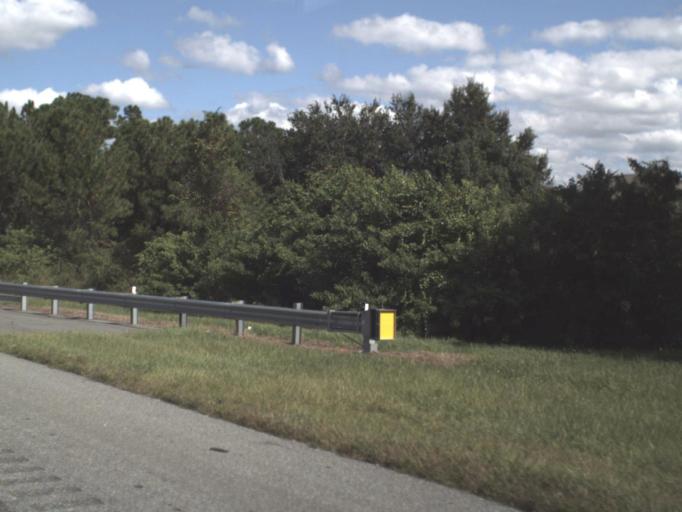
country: US
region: Florida
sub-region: Osceola County
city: Saint Cloud
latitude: 28.2043
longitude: -81.3067
